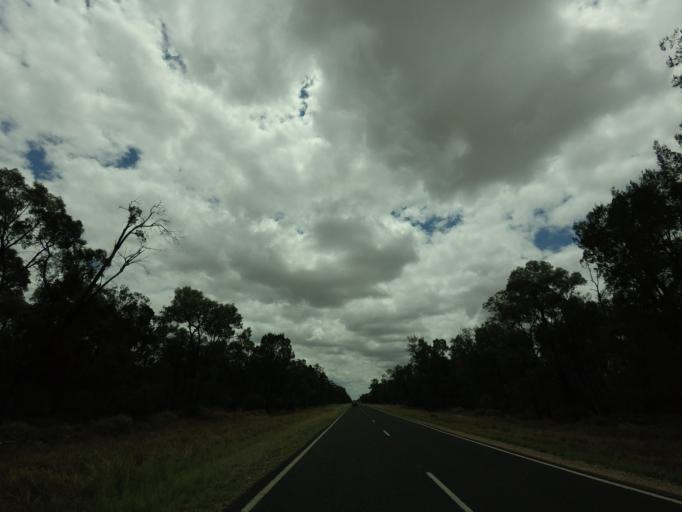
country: AU
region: Queensland
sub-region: Goondiwindi
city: Goondiwindi
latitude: -28.4128
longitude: 150.3049
